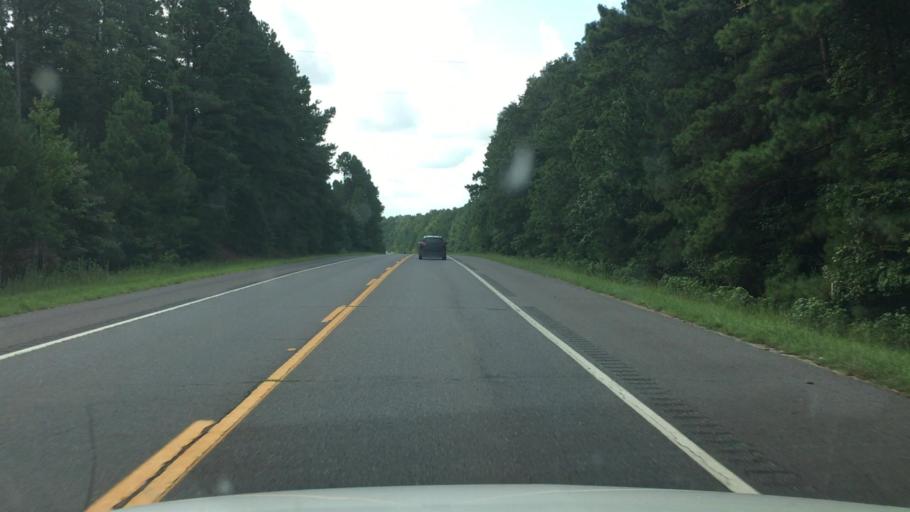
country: US
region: Arkansas
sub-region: Clark County
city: Arkadelphia
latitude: 34.2044
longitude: -93.0786
